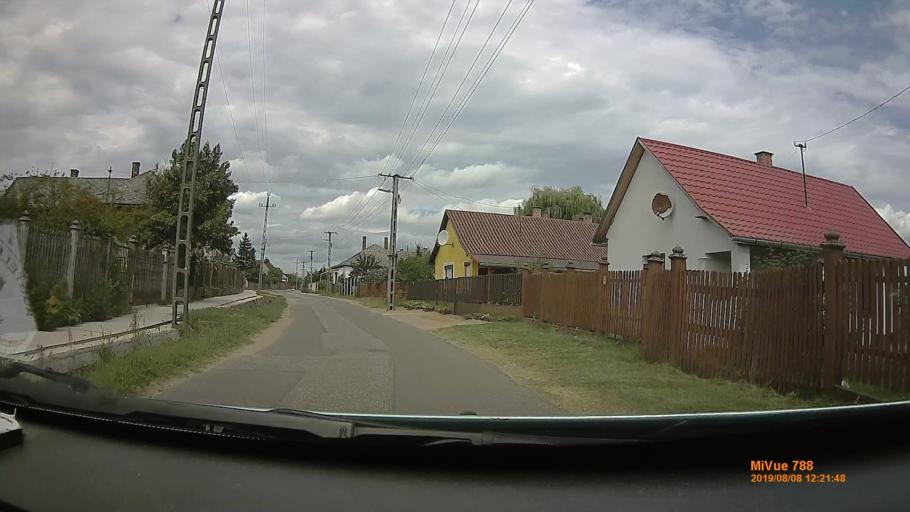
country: HU
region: Szabolcs-Szatmar-Bereg
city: Nyirbogat
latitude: 47.7956
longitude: 22.0558
